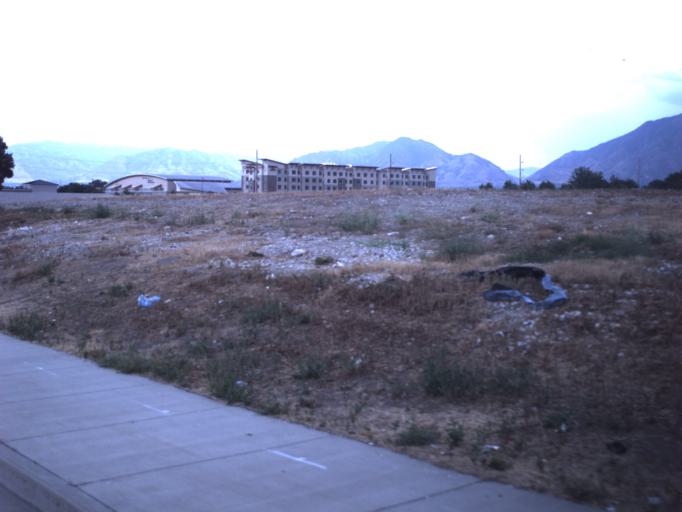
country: US
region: Utah
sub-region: Salt Lake County
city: Murray
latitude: 40.6540
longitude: -111.8882
